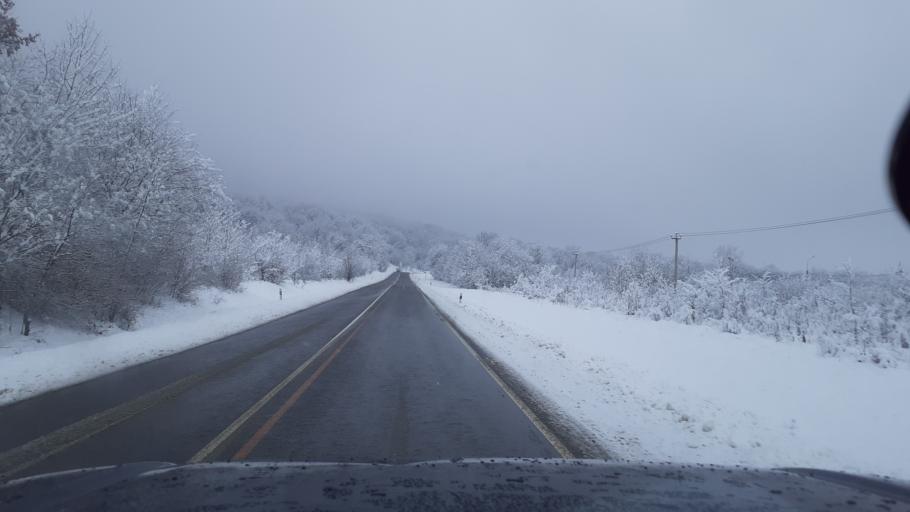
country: RU
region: Adygeya
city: Kamennomostskiy
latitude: 44.2108
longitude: 40.1993
